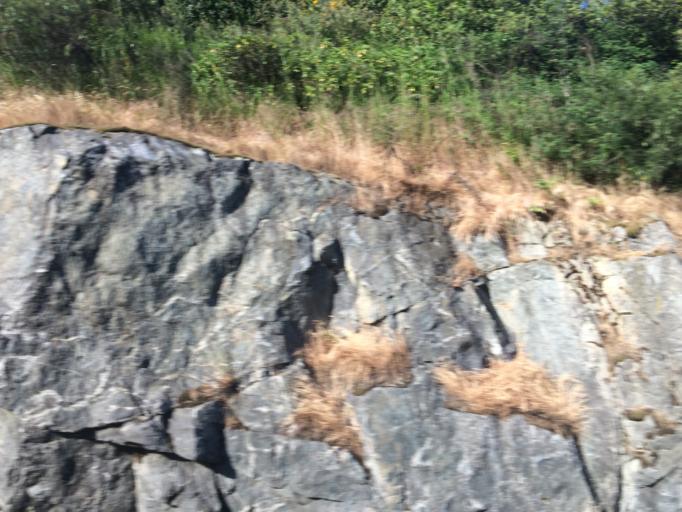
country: CA
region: British Columbia
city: Victoria
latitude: 48.4625
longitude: -123.4128
